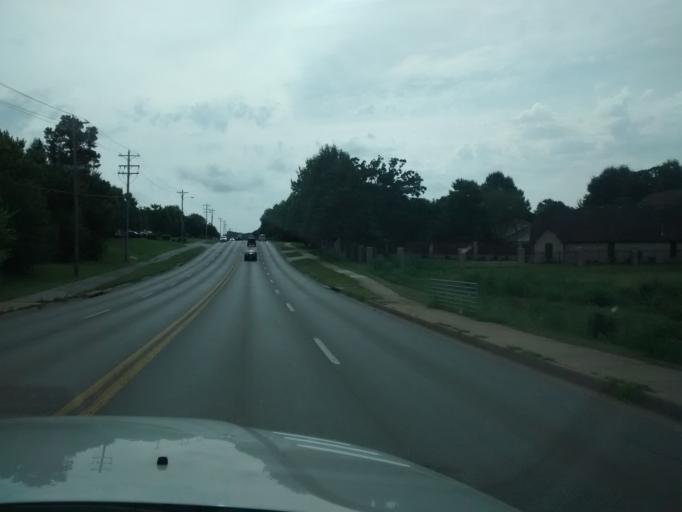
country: US
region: Arkansas
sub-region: Washington County
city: Johnson
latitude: 36.1200
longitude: -94.1280
